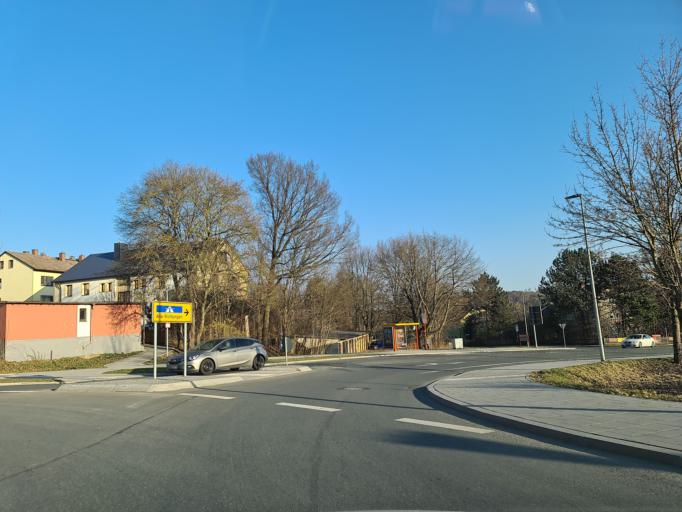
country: DE
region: Bavaria
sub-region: Upper Franconia
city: Dohlau
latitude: 50.2892
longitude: 11.9249
